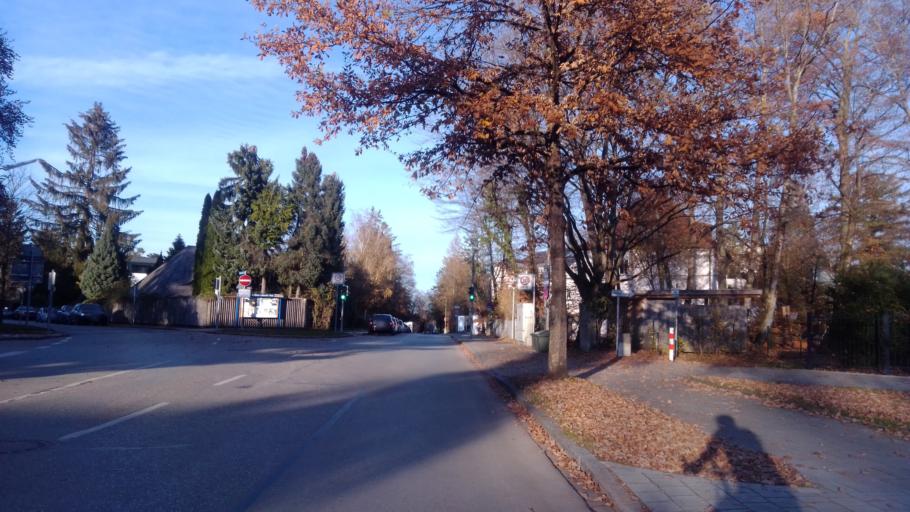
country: DE
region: Bavaria
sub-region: Upper Bavaria
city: Pullach im Isartal
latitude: 48.0714
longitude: 11.5354
